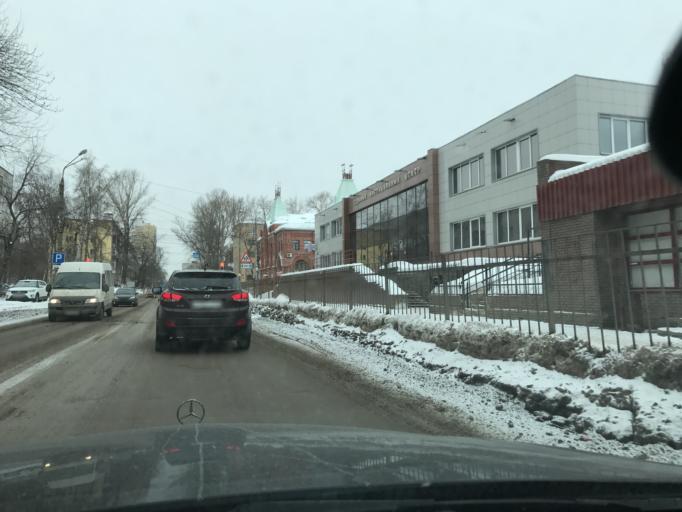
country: RU
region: Nizjnij Novgorod
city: Nizhniy Novgorod
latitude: 56.3318
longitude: 43.9609
